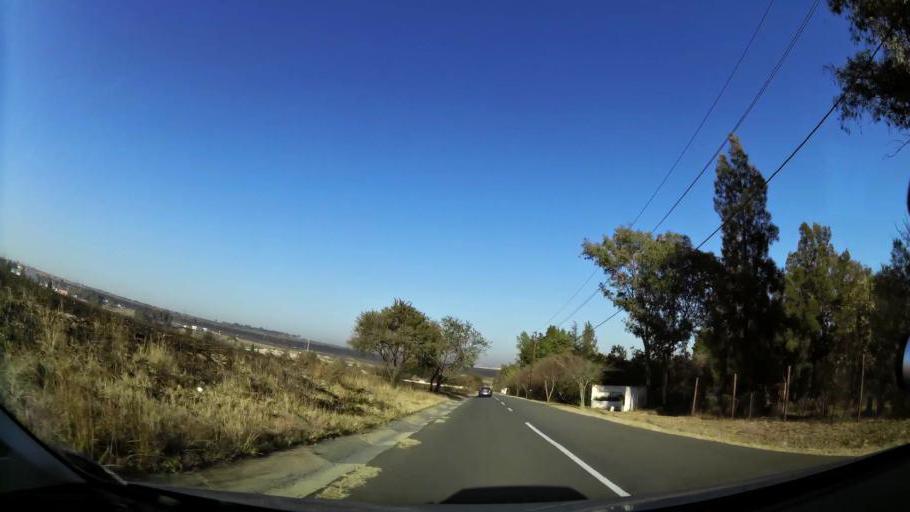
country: ZA
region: Gauteng
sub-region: City of Johannesburg Metropolitan Municipality
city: Midrand
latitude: -26.0257
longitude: 28.1380
